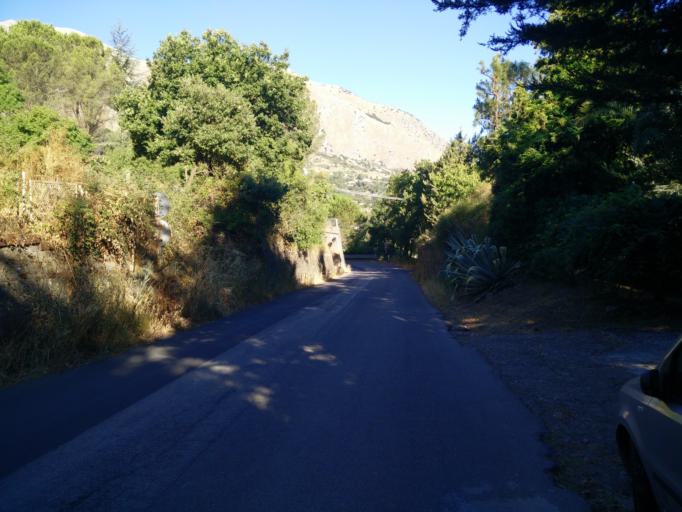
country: IT
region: Sicily
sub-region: Palermo
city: Castelbuono
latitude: 37.9216
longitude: 14.0899
